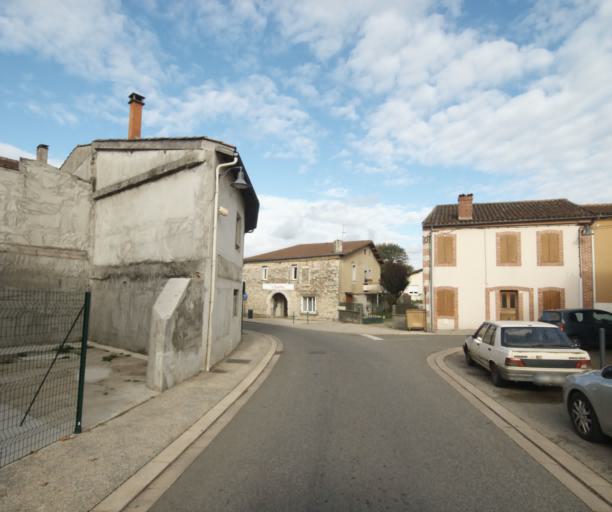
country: FR
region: Midi-Pyrenees
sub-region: Departement du Gers
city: Eauze
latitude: 43.8599
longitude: 0.1028
